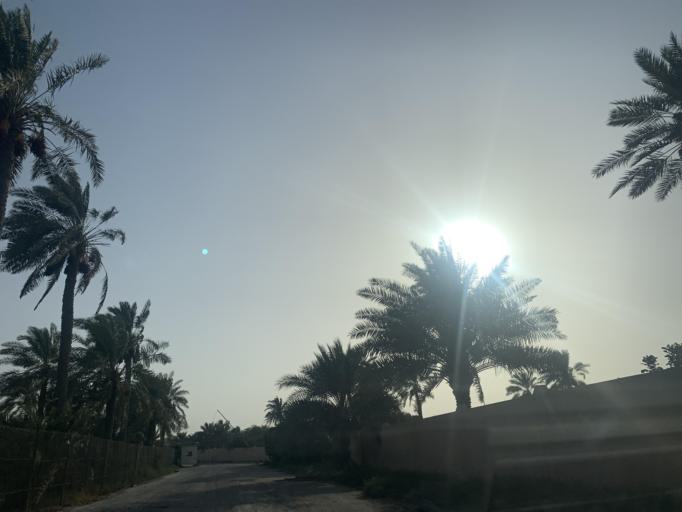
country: BH
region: Central Governorate
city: Madinat Hamad
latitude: 26.1841
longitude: 50.4628
